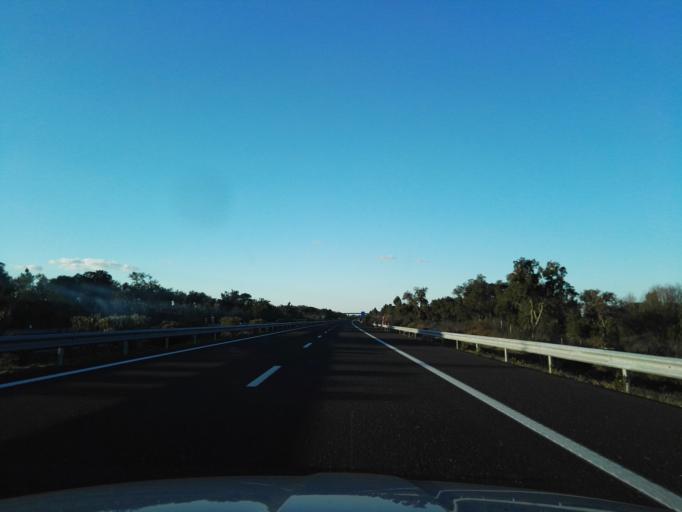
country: PT
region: Santarem
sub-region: Benavente
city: Poceirao
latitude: 38.8189
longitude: -8.7117
